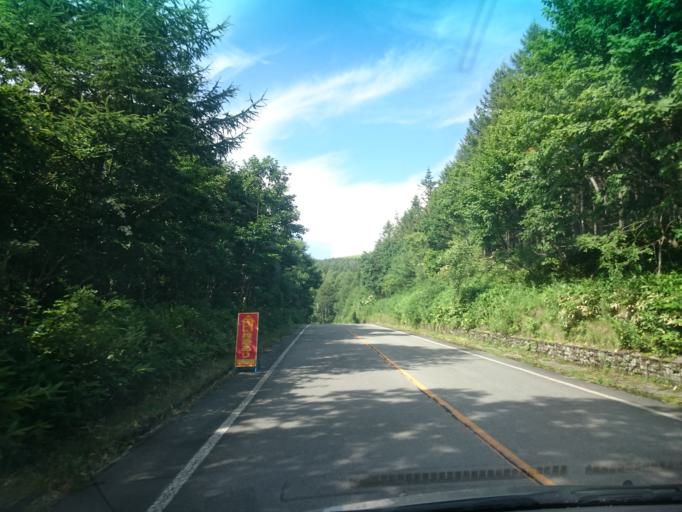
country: JP
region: Nagano
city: Suwa
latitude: 36.1074
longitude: 138.1770
